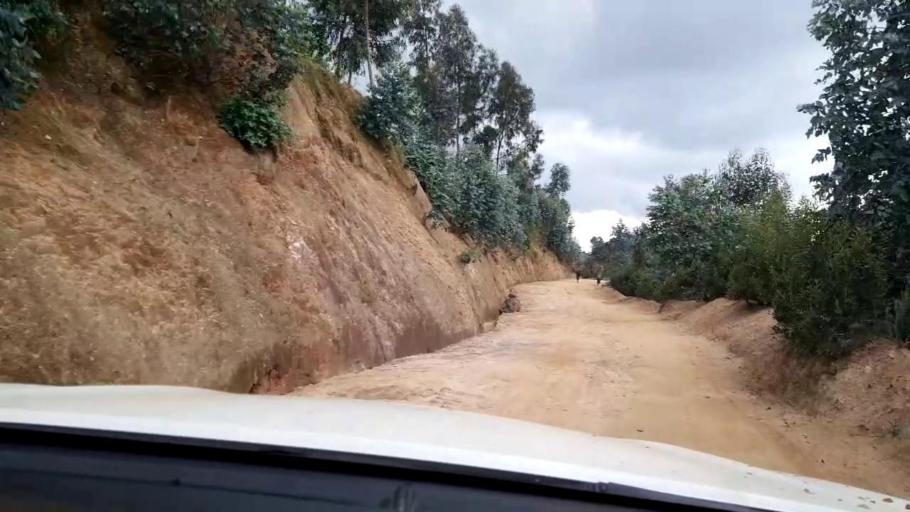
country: RW
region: Western Province
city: Kibuye
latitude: -1.8954
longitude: 29.5282
